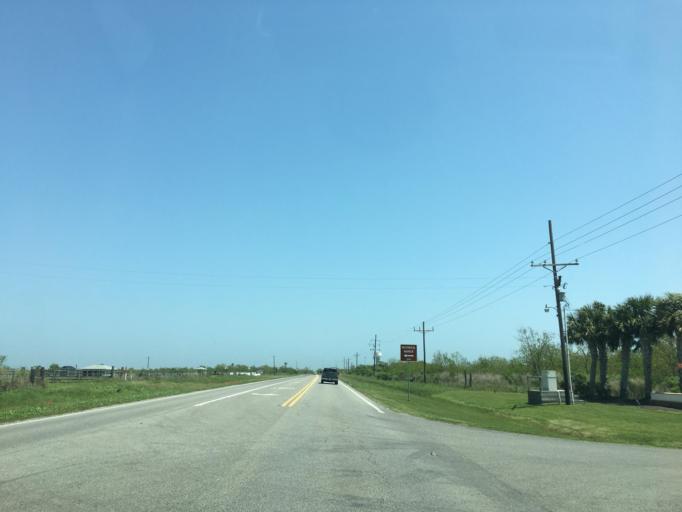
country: US
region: Texas
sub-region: Galveston County
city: Galveston
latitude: 29.4137
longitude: -94.7120
